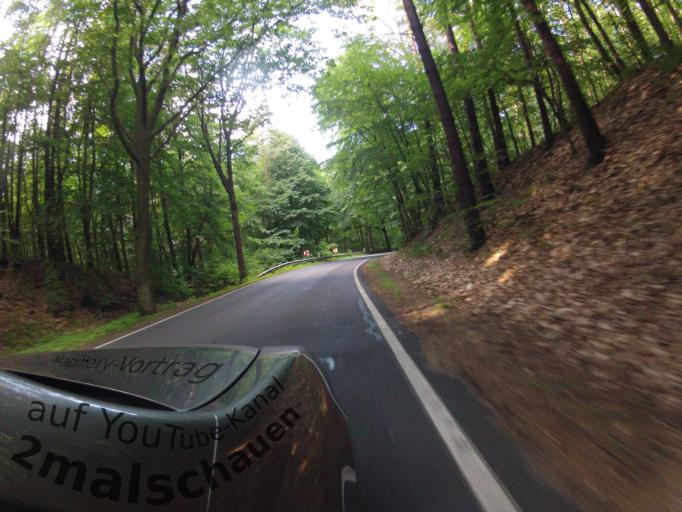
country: DE
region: Mecklenburg-Vorpommern
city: Seebad Heringsdorf
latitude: 53.9298
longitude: 14.1845
